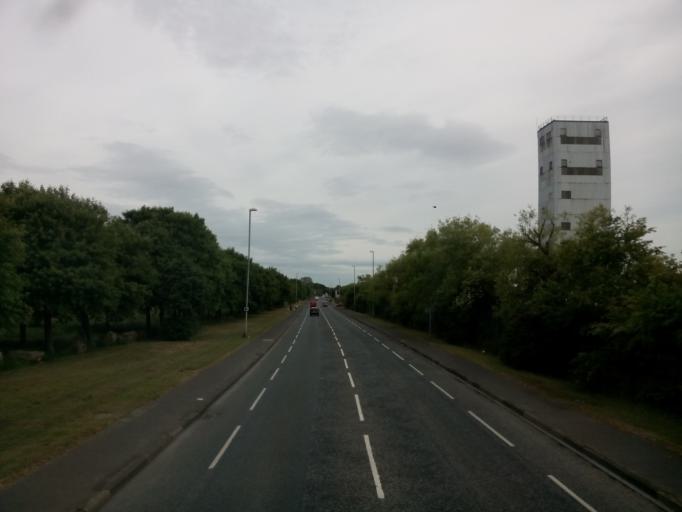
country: GB
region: England
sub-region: County Durham
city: Chester-le-Street
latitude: 54.8861
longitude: -1.5764
